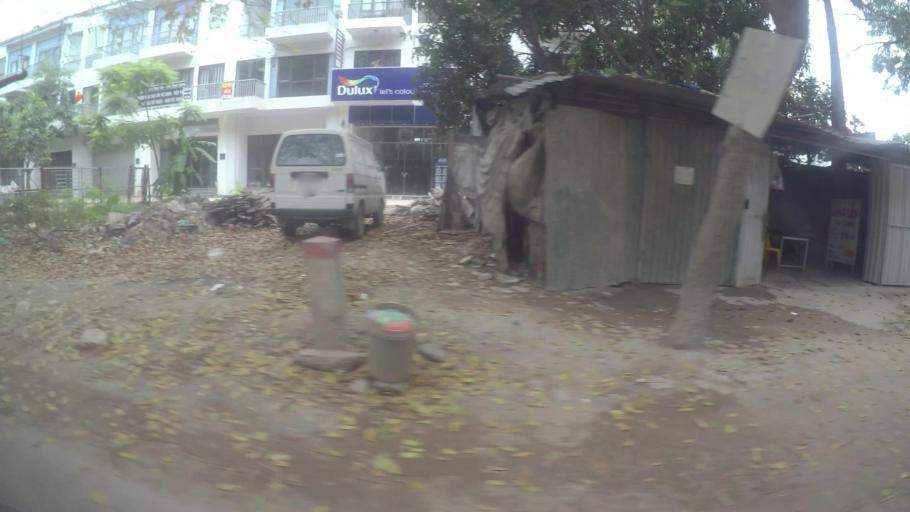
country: VN
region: Ha Noi
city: Cau Dien
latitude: 21.0248
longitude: 105.7421
